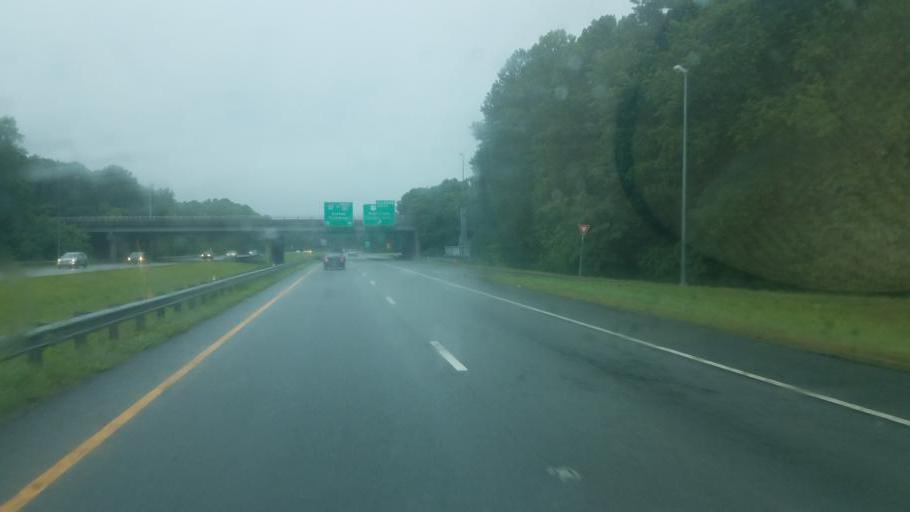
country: US
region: Virginia
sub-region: City of Portsmouth
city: Portsmouth Heights
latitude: 36.7588
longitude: -76.3432
